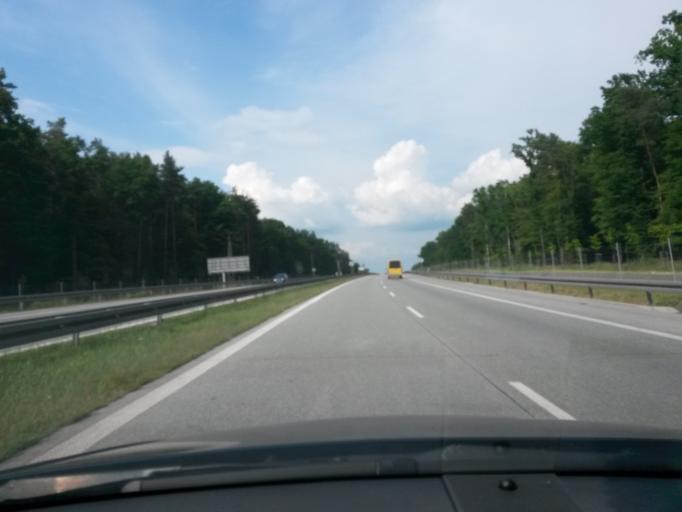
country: PL
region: Lodz Voivodeship
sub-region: Powiat tomaszowski
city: Lubochnia
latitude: 51.5810
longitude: 20.0312
